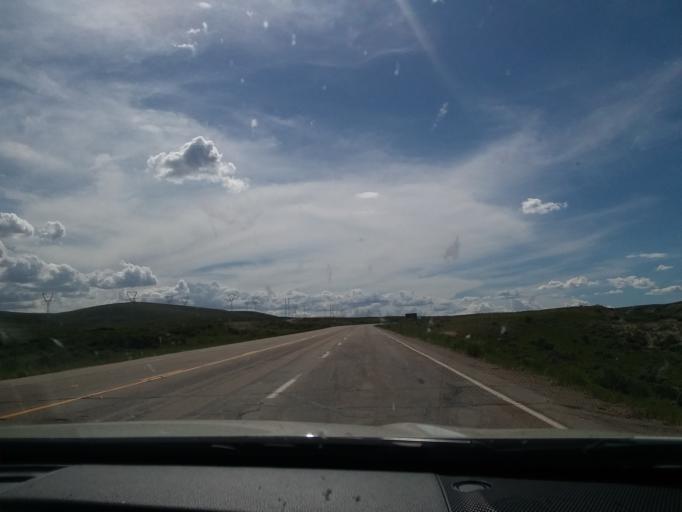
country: US
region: Wyoming
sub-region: Sweetwater County
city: North Rock Springs
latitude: 41.7439
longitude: -109.3175
